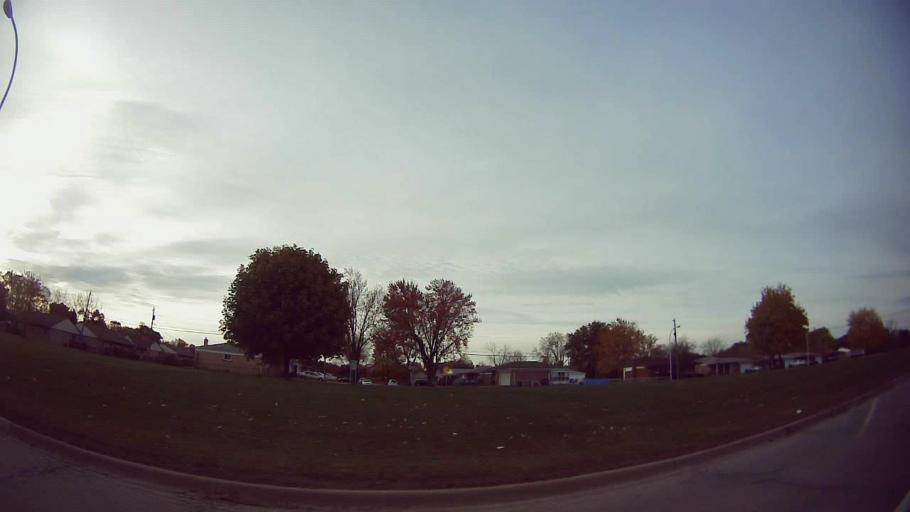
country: US
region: Michigan
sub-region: Macomb County
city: Center Line
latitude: 42.4915
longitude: -83.0519
